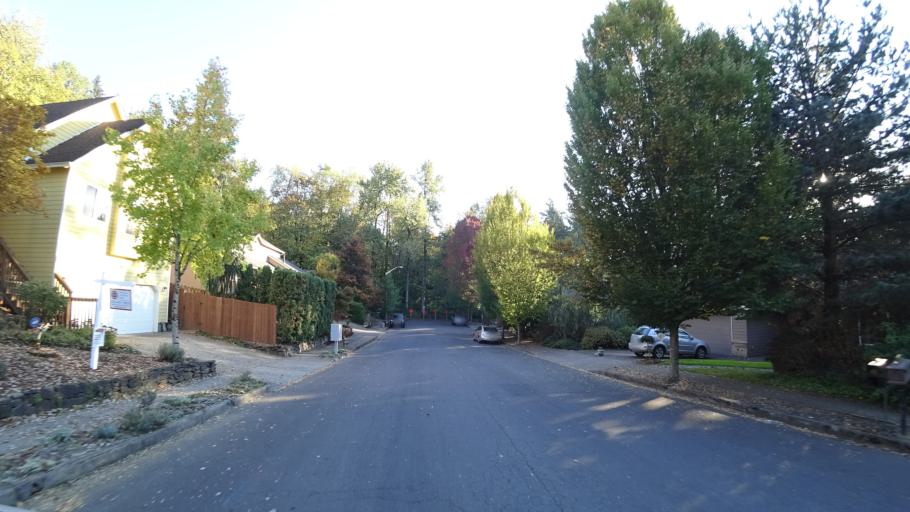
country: US
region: Oregon
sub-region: Multnomah County
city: Gresham
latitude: 45.4856
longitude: -122.4446
